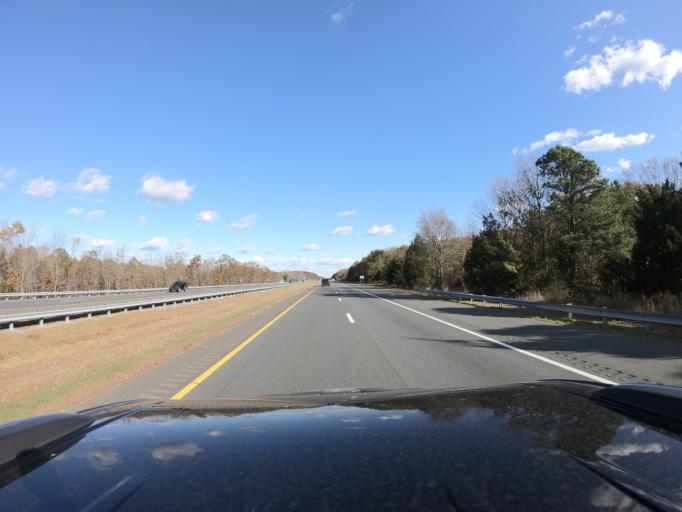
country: US
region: New Jersey
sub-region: Monmouth County
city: Farmingdale
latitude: 40.1667
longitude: -74.2230
